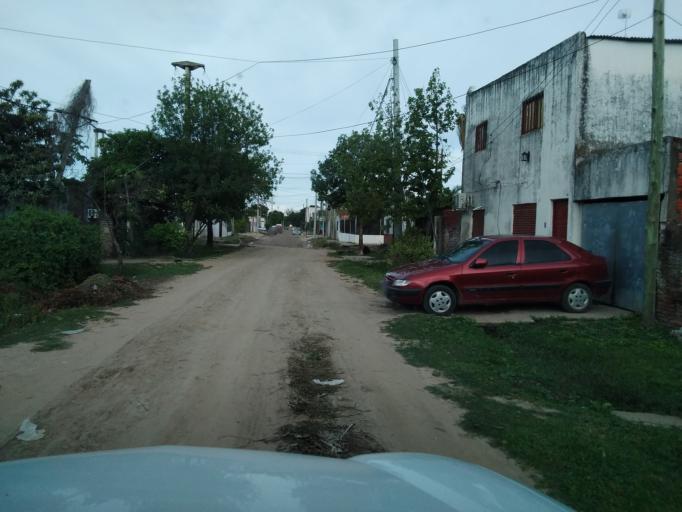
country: AR
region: Corrientes
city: Corrientes
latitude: -27.4914
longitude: -58.8476
